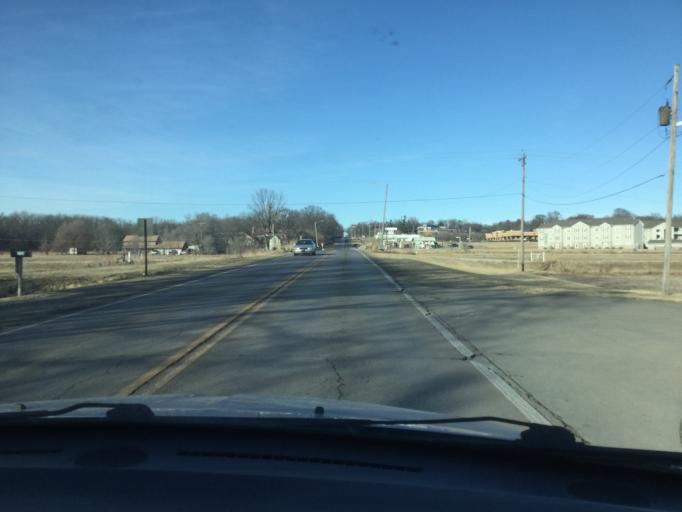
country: US
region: Kansas
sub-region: Shawnee County
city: Topeka
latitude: 39.0965
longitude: -95.6646
